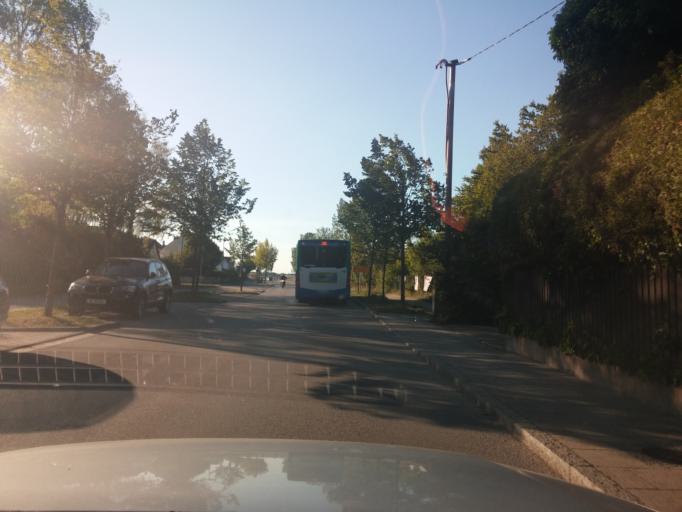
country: DE
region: Bavaria
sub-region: Upper Bavaria
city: Feldkirchen
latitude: 48.1309
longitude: 11.7390
